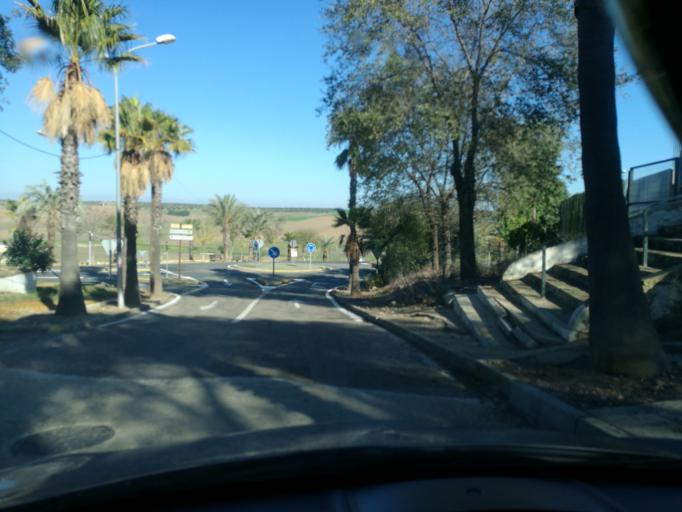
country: ES
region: Andalusia
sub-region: Provincia de Sevilla
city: La Campana
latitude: 37.5707
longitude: -5.4238
